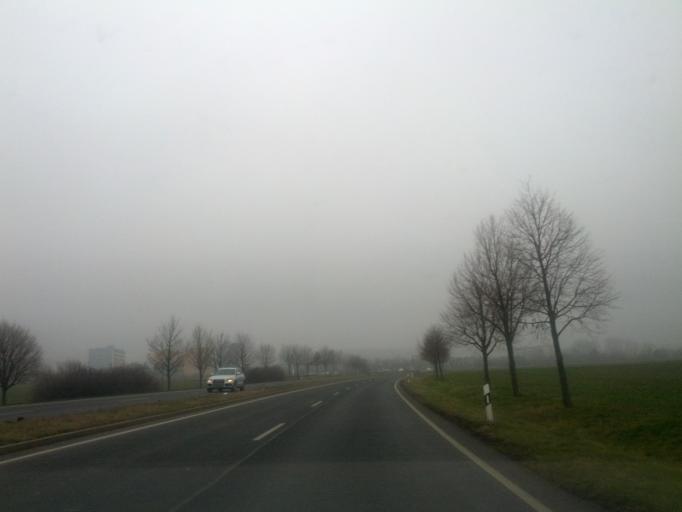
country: DE
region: Thuringia
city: Erfurt
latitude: 50.9589
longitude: 11.0861
